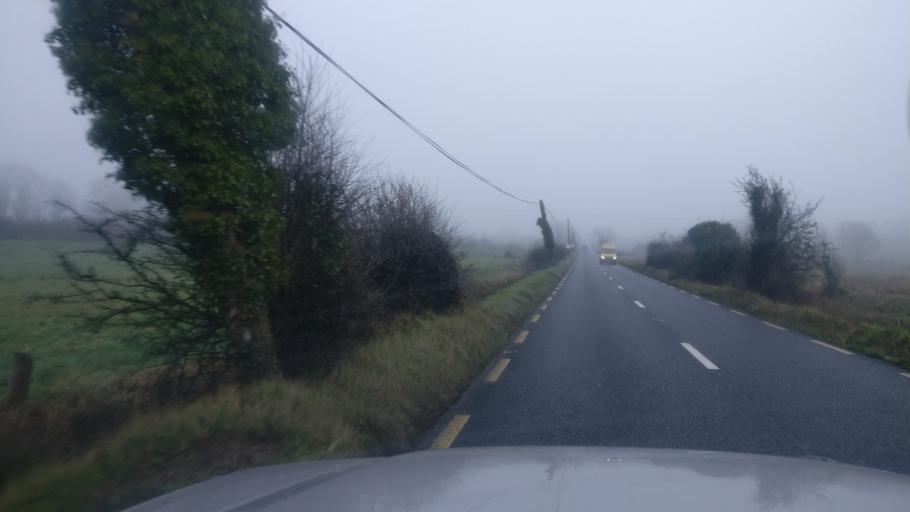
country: IE
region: Connaught
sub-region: County Galway
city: Loughrea
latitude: 53.1864
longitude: -8.6212
